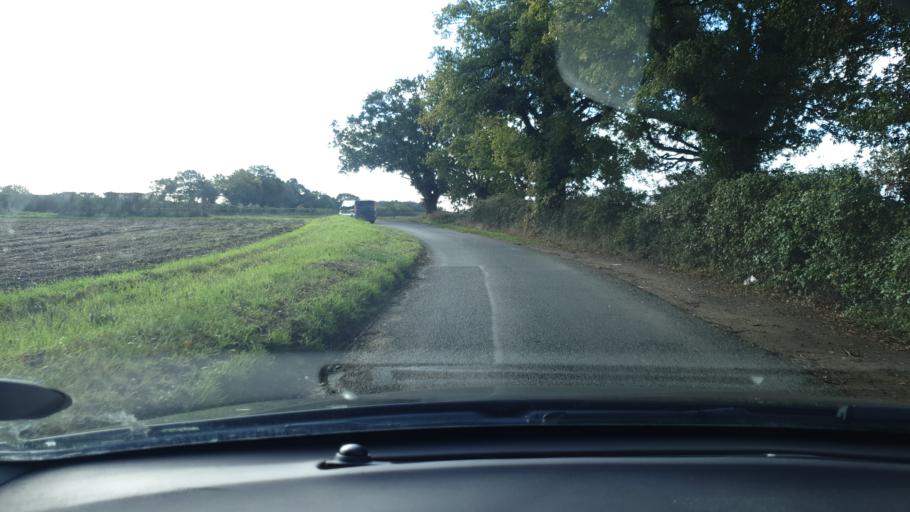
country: GB
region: England
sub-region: Essex
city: Alresford
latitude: 51.8679
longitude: 1.0157
